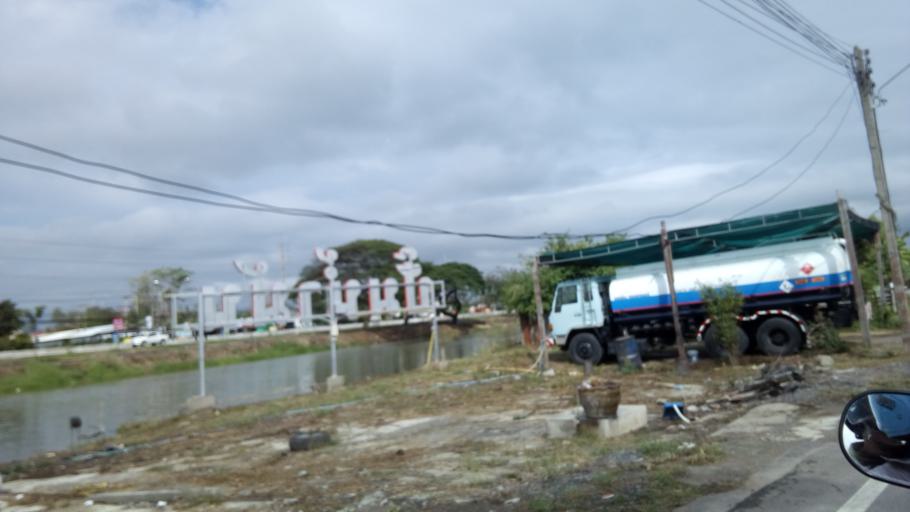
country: TH
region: Pathum Thani
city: Nong Suea
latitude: 14.0669
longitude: 100.8669
